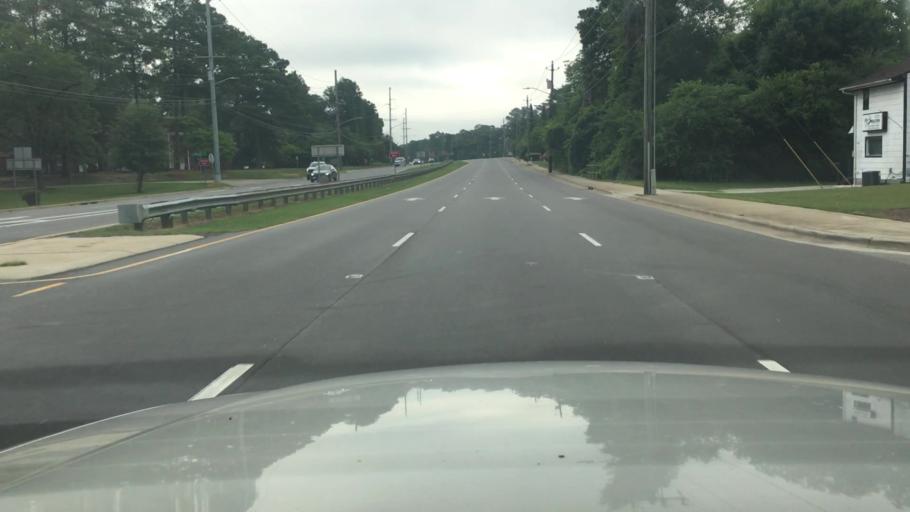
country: US
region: North Carolina
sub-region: Cumberland County
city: Fayetteville
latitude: 35.0711
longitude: -78.9206
